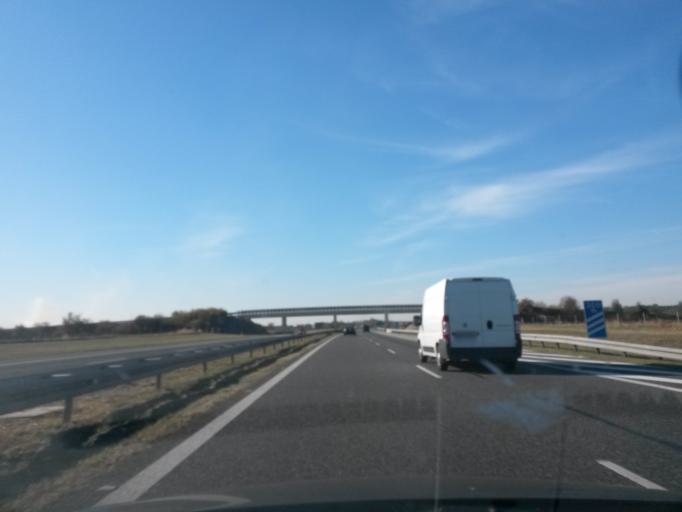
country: PL
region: Opole Voivodeship
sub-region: Powiat brzeski
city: Grodkow
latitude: 50.7766
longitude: 17.3596
